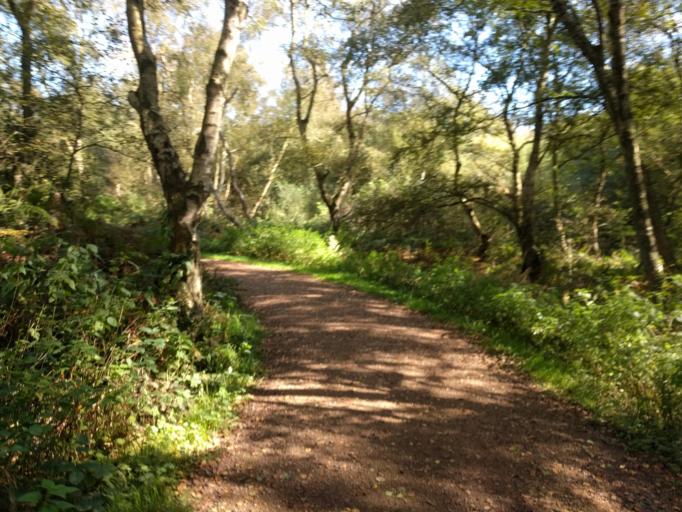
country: GB
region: England
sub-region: Warrington
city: Culcheth
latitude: 53.4199
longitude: -2.5074
